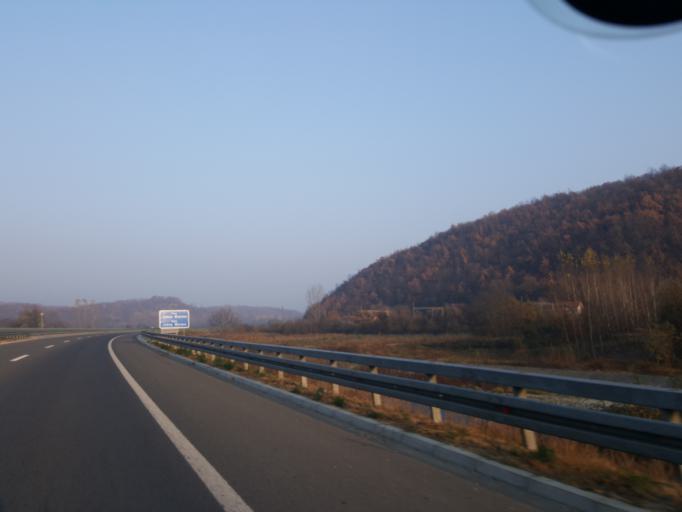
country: RS
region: Central Serbia
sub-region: Jablanicki Okrug
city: Vlasotince
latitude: 42.8940
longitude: 22.0560
